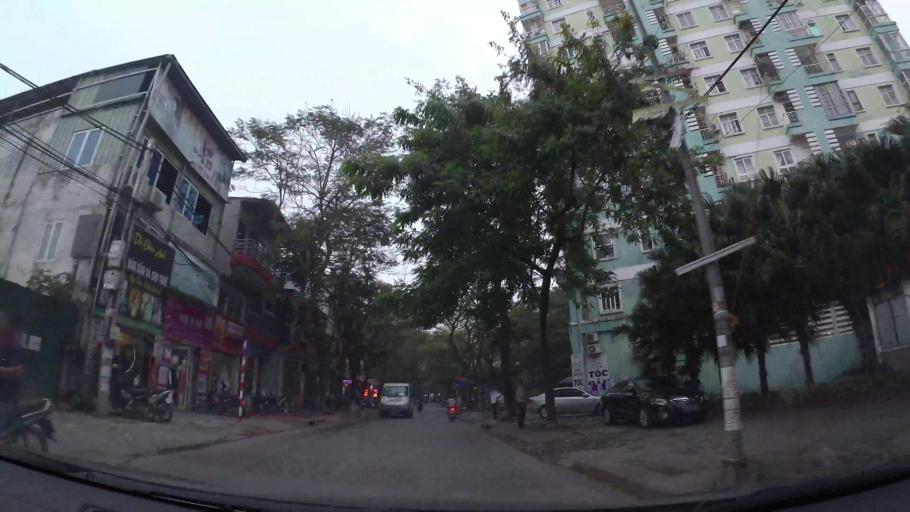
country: VN
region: Ha Noi
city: Hai BaTrung
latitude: 20.9898
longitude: 105.8304
